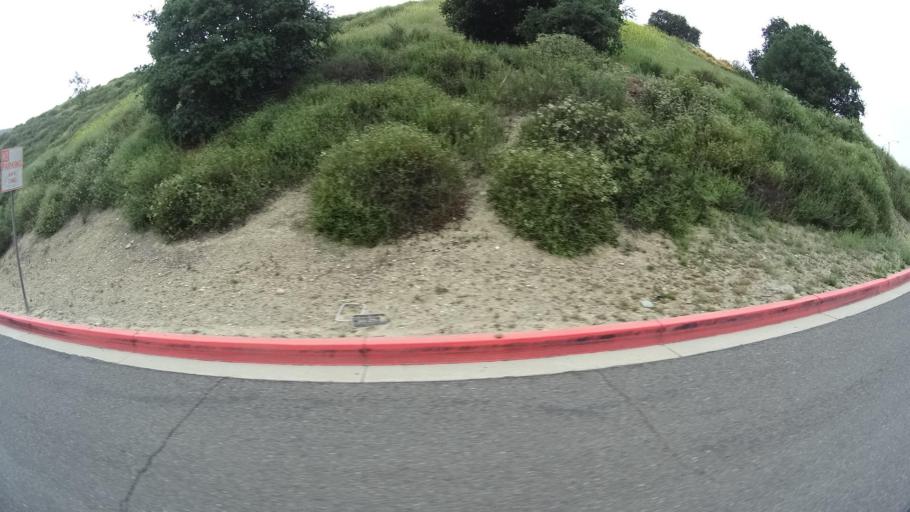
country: US
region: California
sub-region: San Bernardino County
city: Chino Hills
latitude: 34.0221
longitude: -117.7725
